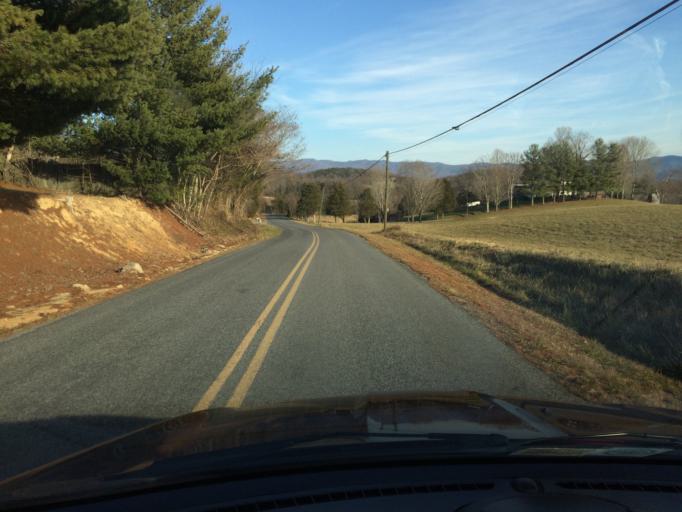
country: US
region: Virginia
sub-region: Botetourt County
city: Fincastle
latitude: 37.6194
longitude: -79.8340
